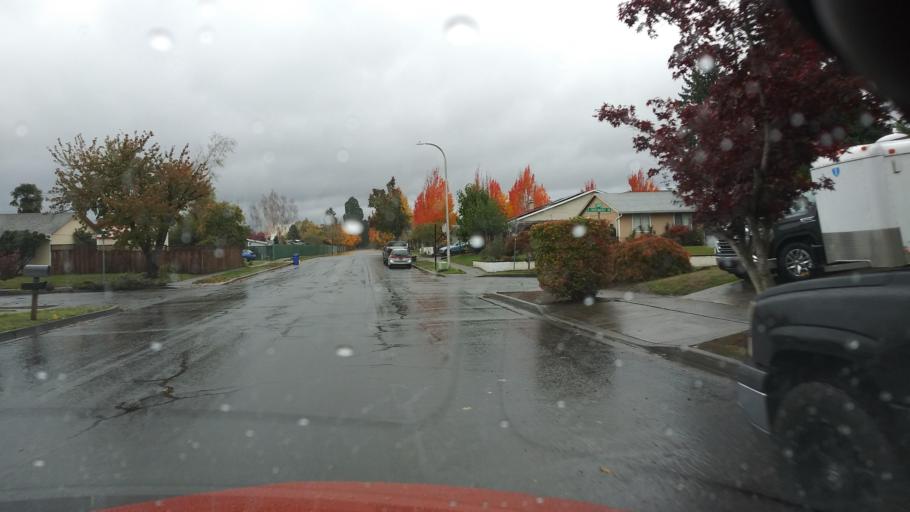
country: US
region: Oregon
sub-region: Washington County
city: Cornelius
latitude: 45.5140
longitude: -123.0696
